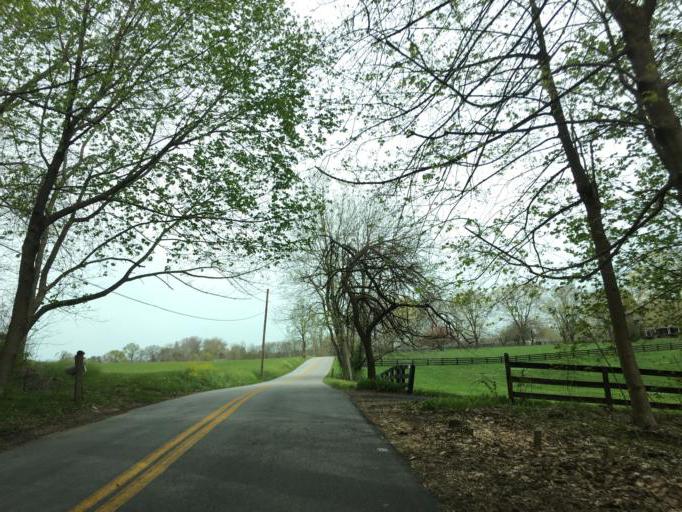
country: US
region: Maryland
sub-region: Baltimore County
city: Hunt Valley
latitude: 39.5471
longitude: -76.6187
